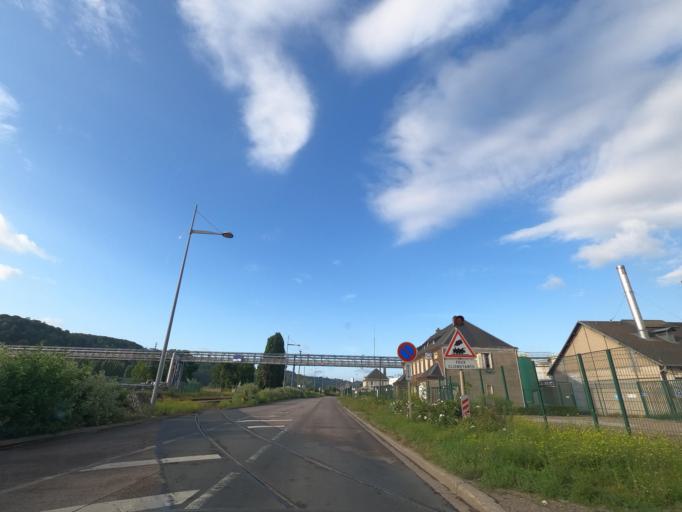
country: FR
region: Haute-Normandie
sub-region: Departement de la Seine-Maritime
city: Petit-Couronne
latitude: 49.4103
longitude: 1.0176
